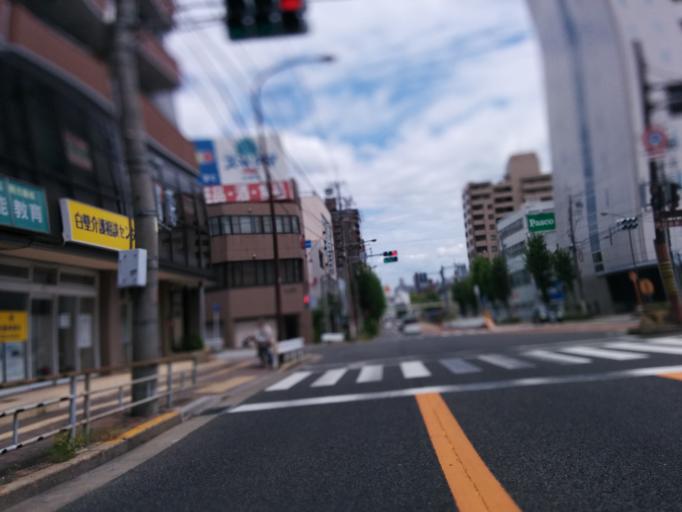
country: JP
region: Aichi
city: Nagoya-shi
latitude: 35.1836
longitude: 136.9188
